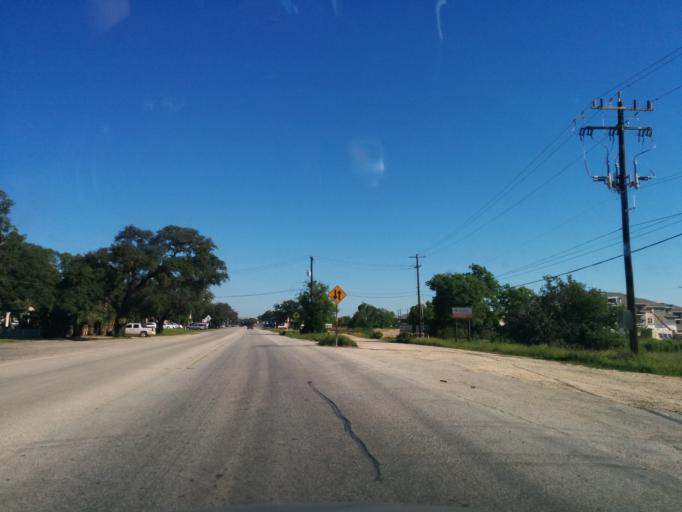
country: US
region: Texas
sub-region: Bexar County
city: Cross Mountain
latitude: 29.6613
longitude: -98.6273
